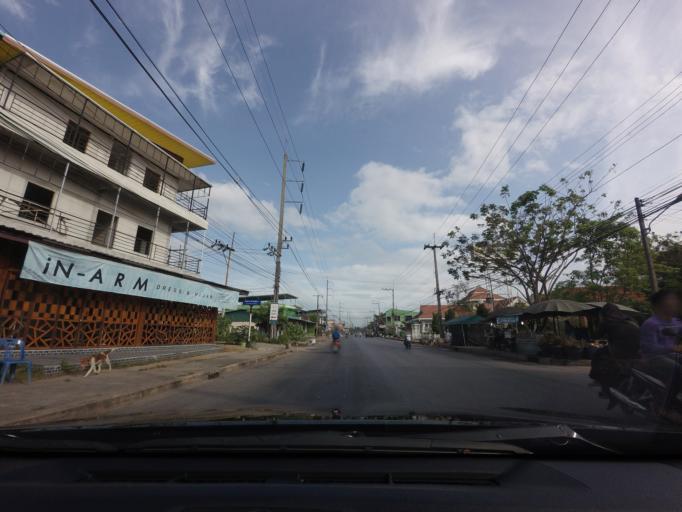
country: TH
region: Yala
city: Yala
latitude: 6.5241
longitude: 101.2653
